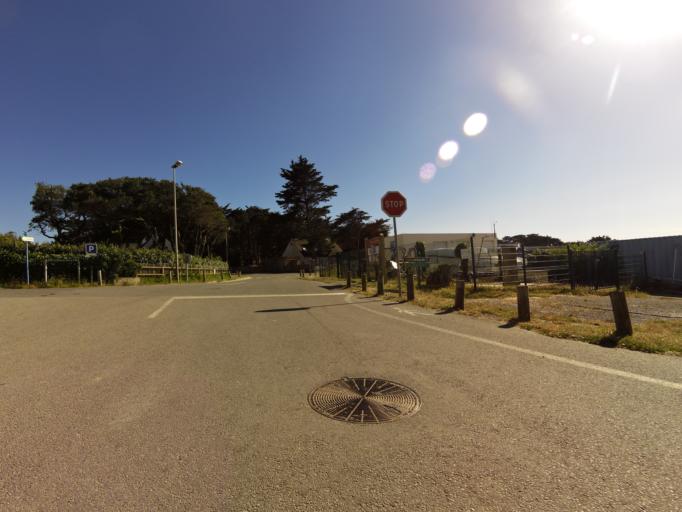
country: FR
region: Brittany
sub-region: Departement du Morbihan
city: Penestin
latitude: 47.4673
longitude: -2.4885
